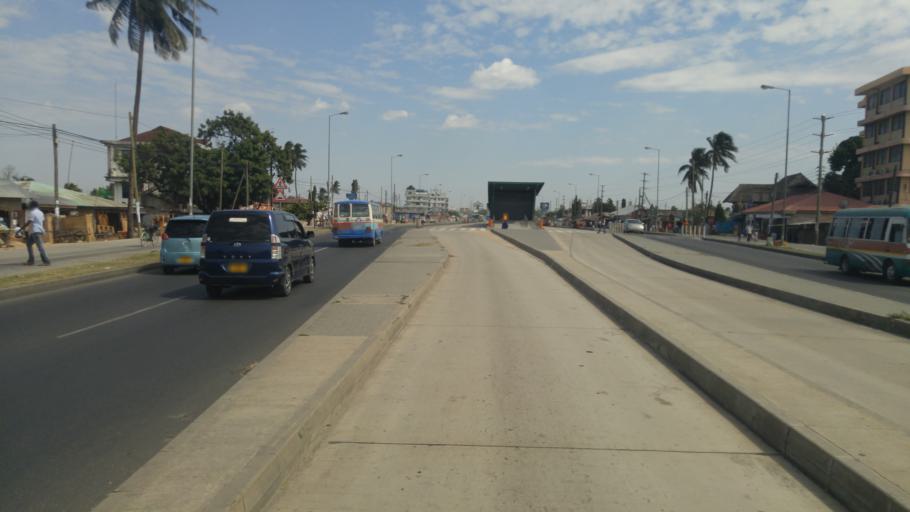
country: TZ
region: Dar es Salaam
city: Magomeni
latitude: -6.8014
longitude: 39.2411
